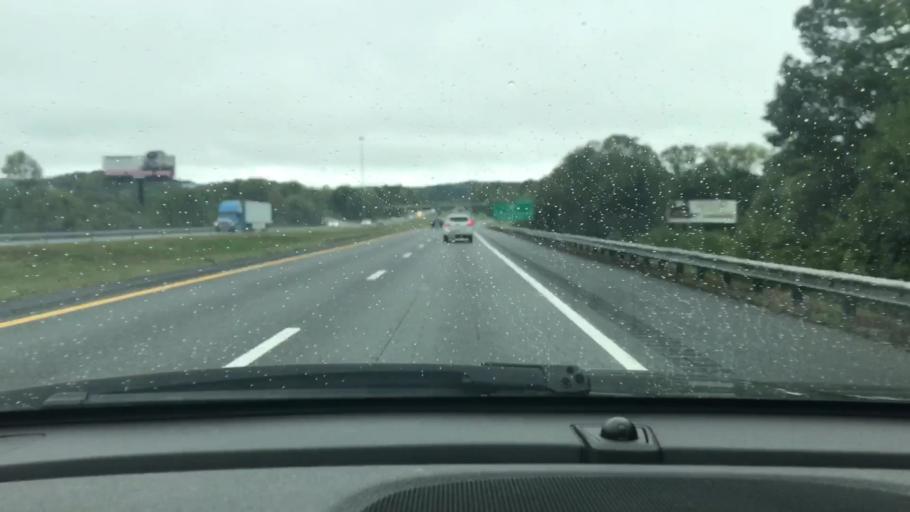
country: US
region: Tennessee
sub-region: Cheatham County
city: Kingston Springs
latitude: 36.0848
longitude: -87.0916
